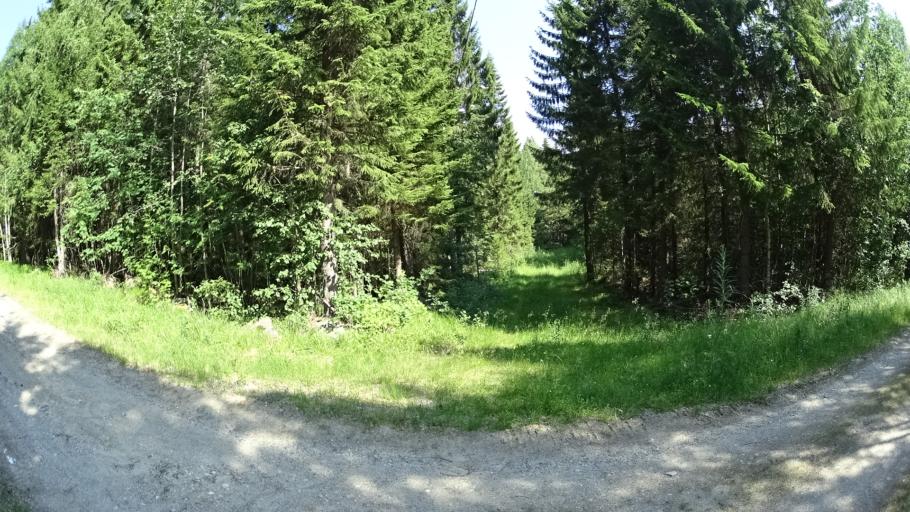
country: FI
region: North Karelia
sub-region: Pielisen Karjala
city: Lieksa
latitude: 63.1154
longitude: 29.7878
